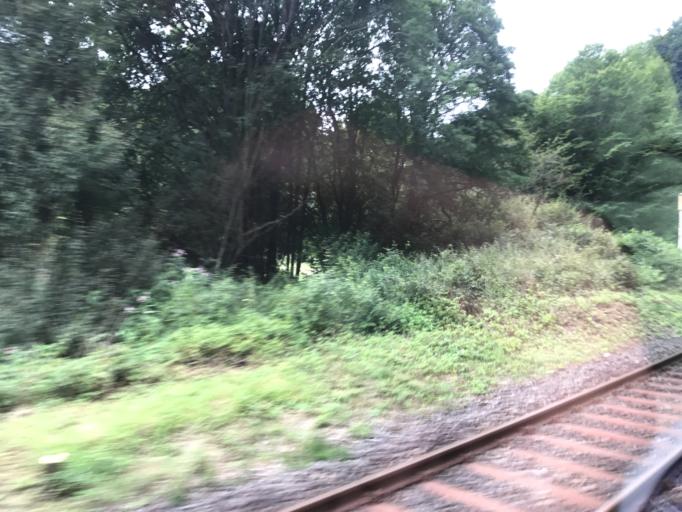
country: DE
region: Hesse
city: Weilburg
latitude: 50.4600
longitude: 8.2522
